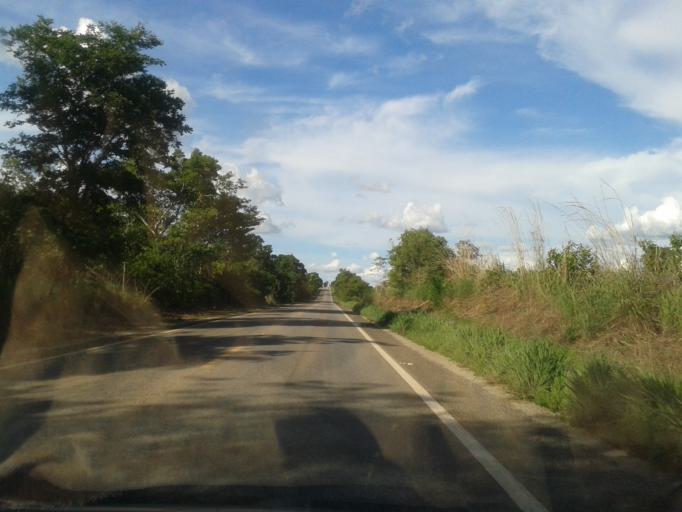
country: BR
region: Goias
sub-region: Mozarlandia
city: Mozarlandia
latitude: -14.5413
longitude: -50.4899
